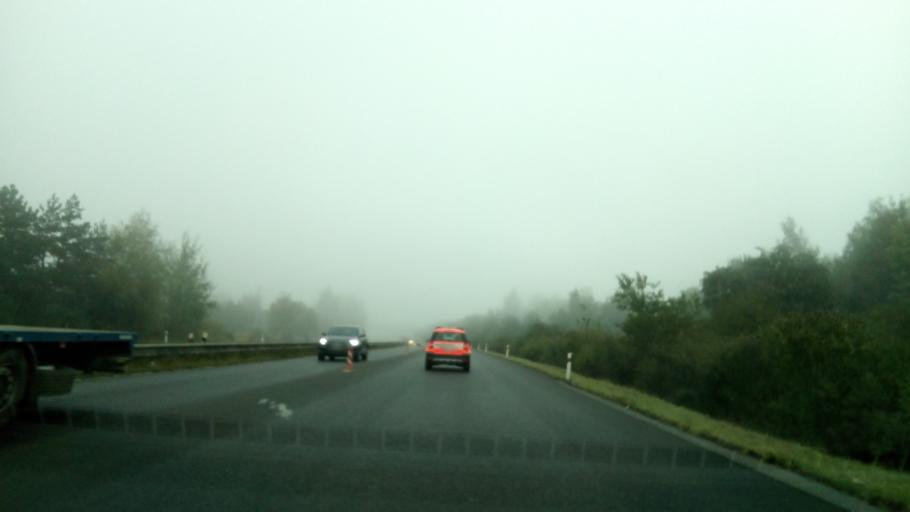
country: CZ
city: Paskov
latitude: 49.7435
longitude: 18.2802
